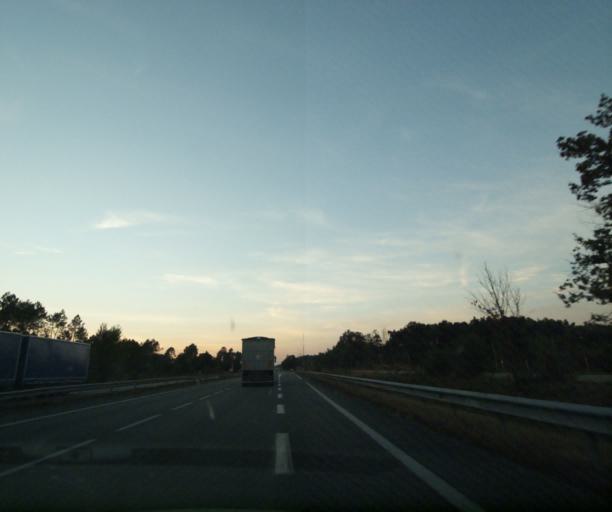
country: FR
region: Aquitaine
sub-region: Departement de la Gironde
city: Portets
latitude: 44.6422
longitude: -0.4301
